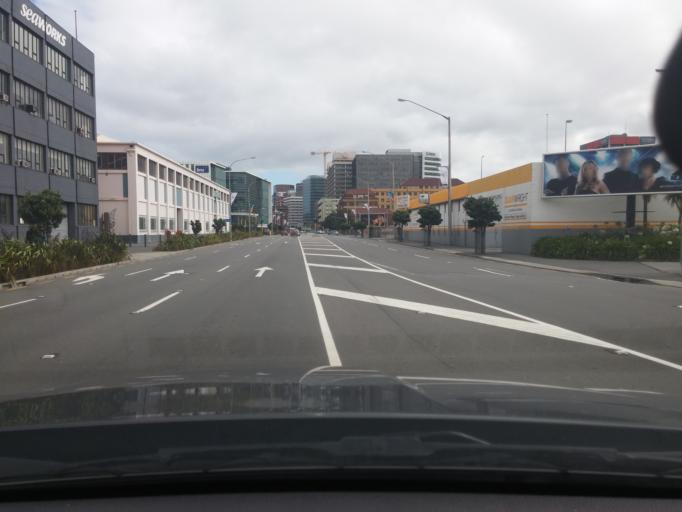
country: NZ
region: Wellington
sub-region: Wellington City
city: Wellington
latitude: -41.2773
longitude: 174.7834
